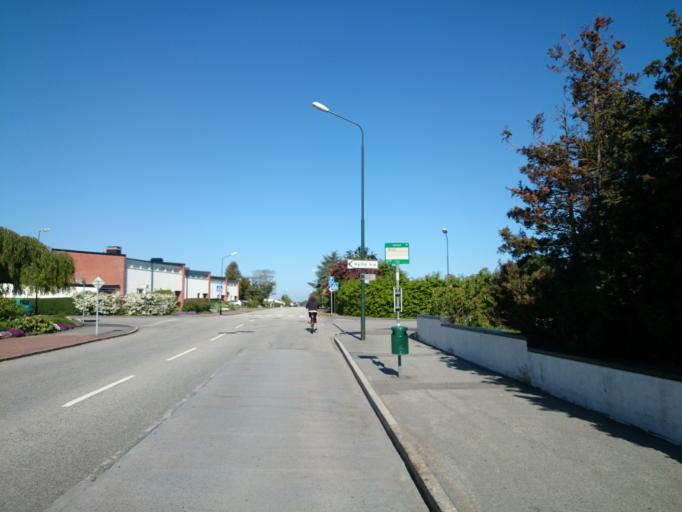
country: SE
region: Skane
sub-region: Malmo
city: Malmoe
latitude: 55.5768
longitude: 12.9720
